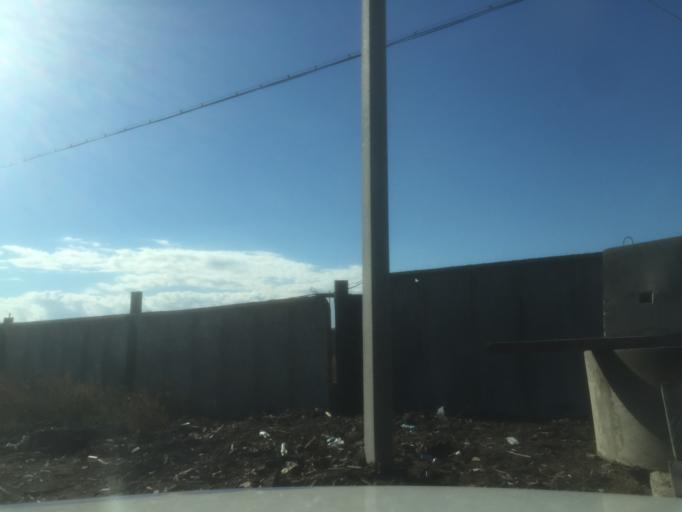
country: KZ
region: Astana Qalasy
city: Astana
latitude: 51.2135
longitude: 71.3503
